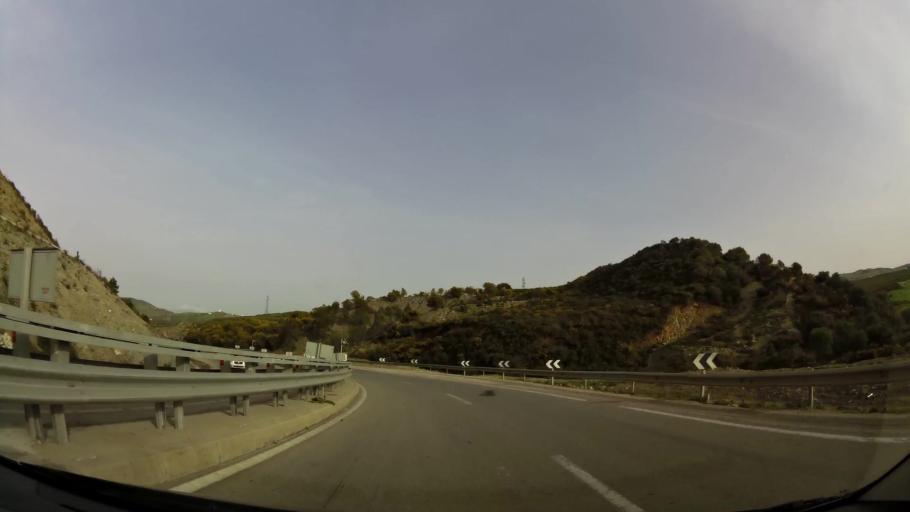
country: MA
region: Tanger-Tetouan
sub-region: Tetouan
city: Saddina
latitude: 35.5486
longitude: -5.5351
